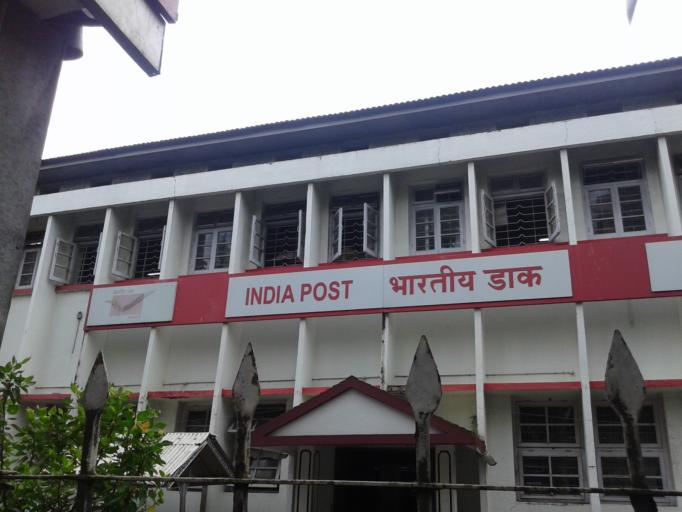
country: IN
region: Kerala
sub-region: Kozhikode
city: Kozhikode
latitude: 11.2559
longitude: 75.7785
